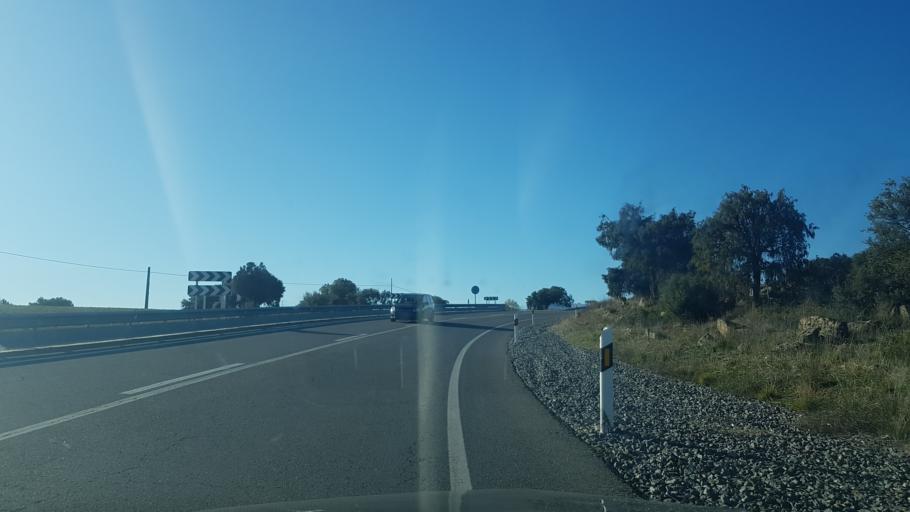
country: ES
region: Castille and Leon
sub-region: Provincia de Avila
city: Barraco
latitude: 40.4562
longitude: -4.6104
